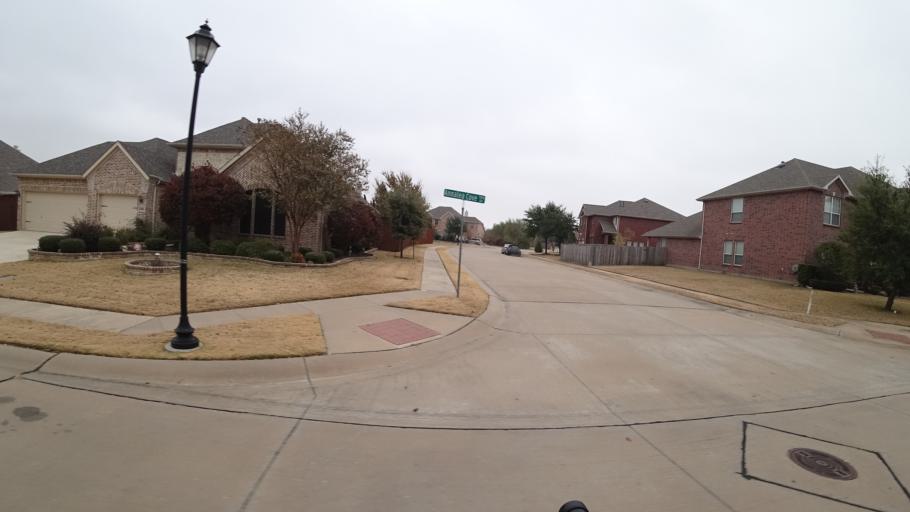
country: US
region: Texas
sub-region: Denton County
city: The Colony
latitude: 33.0703
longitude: -96.9082
